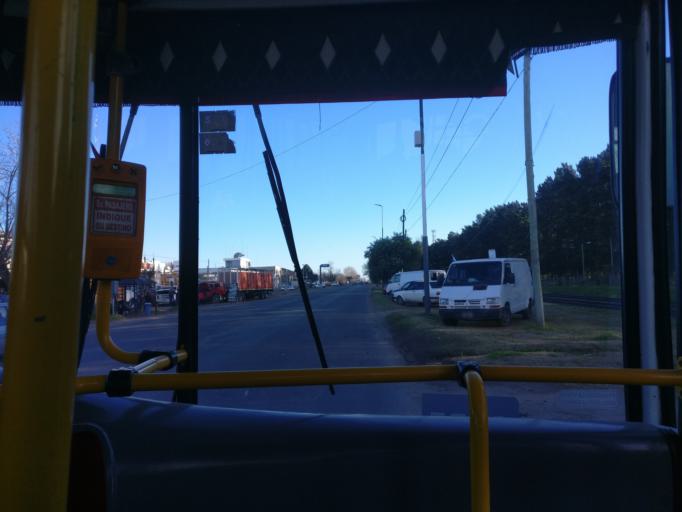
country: AR
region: Buenos Aires
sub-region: Partido de Ezeiza
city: Ezeiza
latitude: -34.8984
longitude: -58.5791
